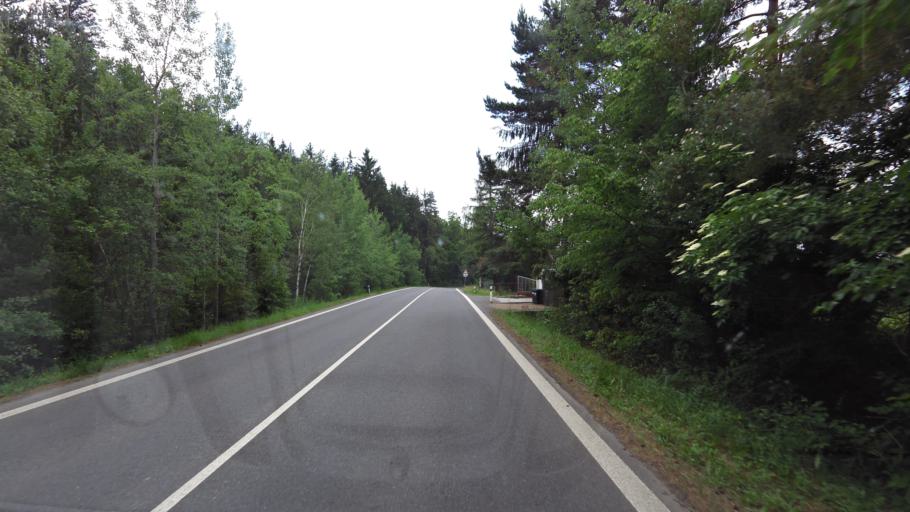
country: CZ
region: Plzensky
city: St'ahlavy
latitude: 49.6967
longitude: 13.5224
